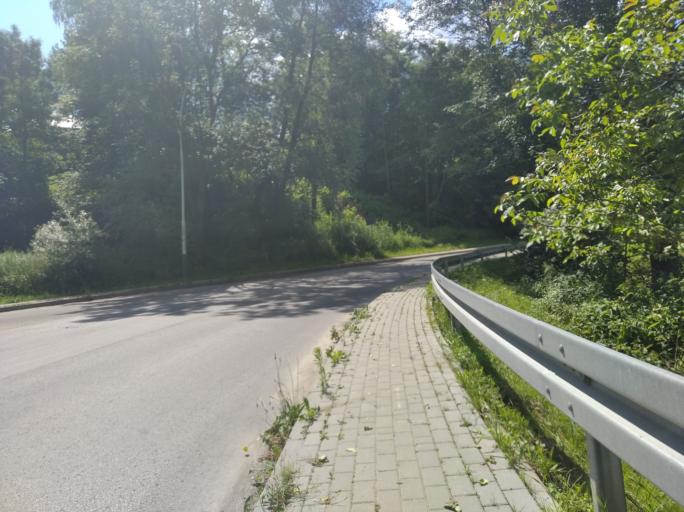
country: PL
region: Subcarpathian Voivodeship
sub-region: Powiat rzeszowski
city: Dynow
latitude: 49.8016
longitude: 22.2456
